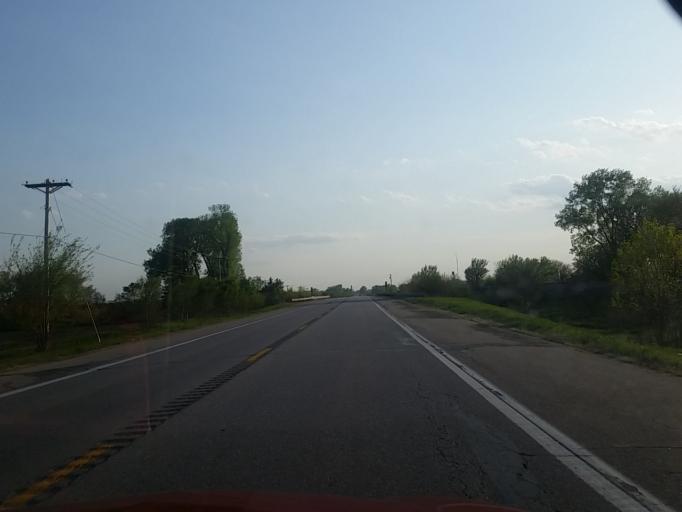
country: US
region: Nebraska
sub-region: Saunders County
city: Ashland
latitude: 41.0765
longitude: -96.3007
